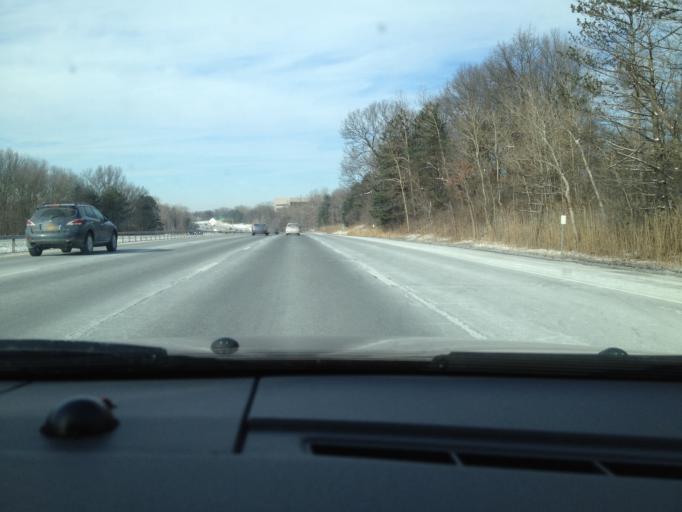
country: US
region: New York
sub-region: Albany County
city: West Albany
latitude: 42.6762
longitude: -73.7618
